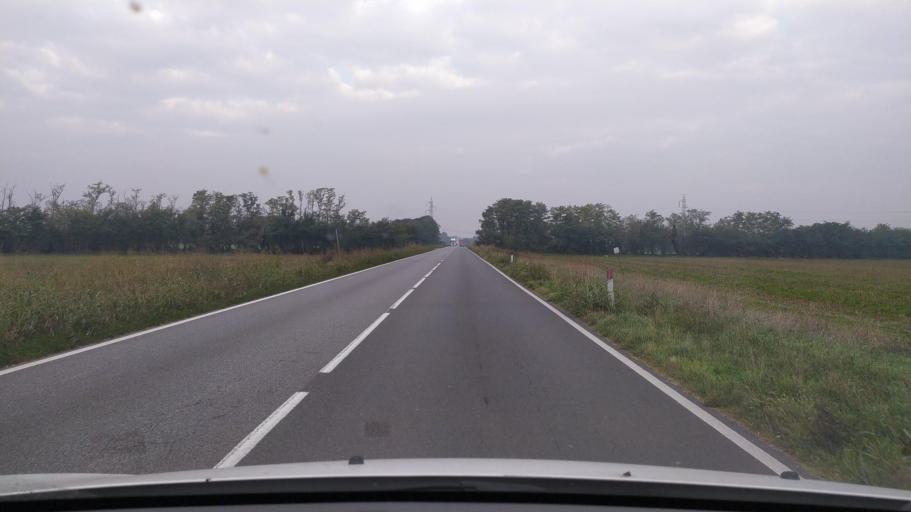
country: IT
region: Lombardy
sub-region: Citta metropolitana di Milano
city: Vittuone
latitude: 45.4696
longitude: 8.9632
